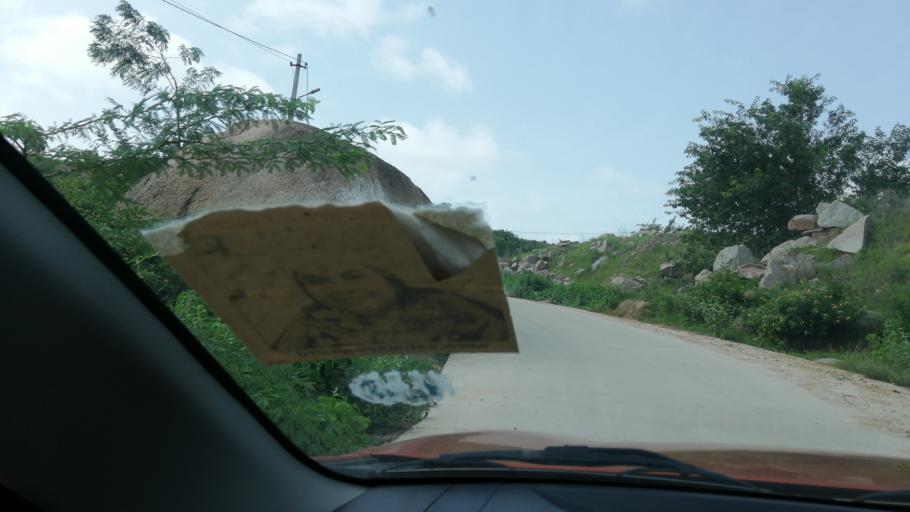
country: IN
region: Telangana
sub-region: Rangareddi
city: Kukatpalli
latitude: 17.4124
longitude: 78.3660
